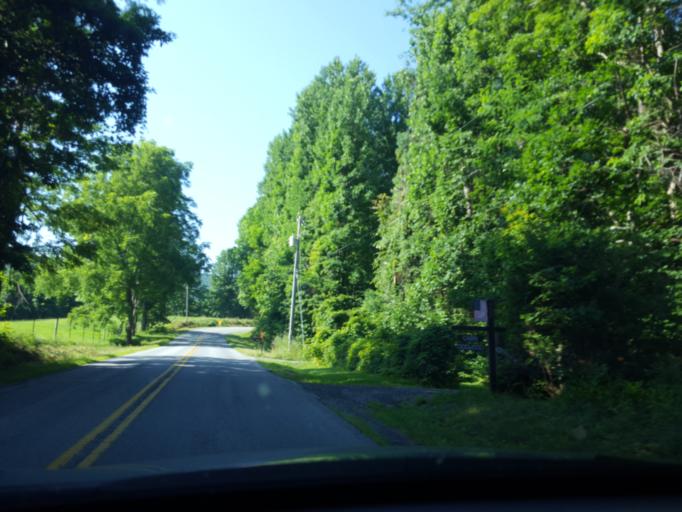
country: US
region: Virginia
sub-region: Nelson County
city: Nellysford
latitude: 37.9123
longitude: -78.9887
